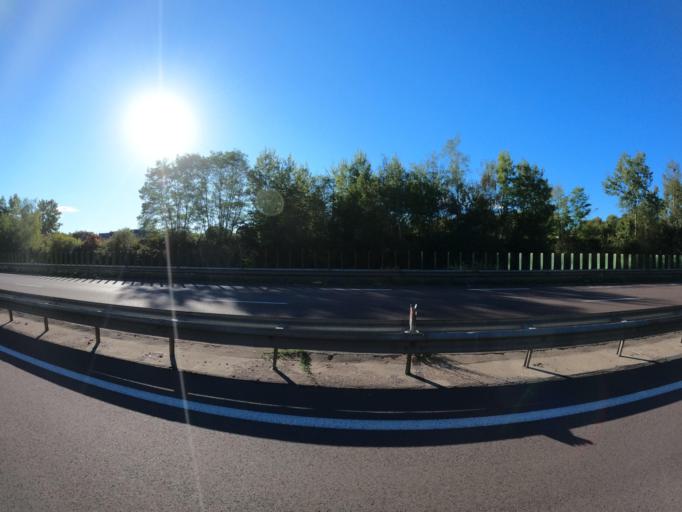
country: FR
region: Bourgogne
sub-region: Departement de Saone-et-Loire
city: Montceau-les-Mines
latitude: 46.6793
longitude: 4.3464
